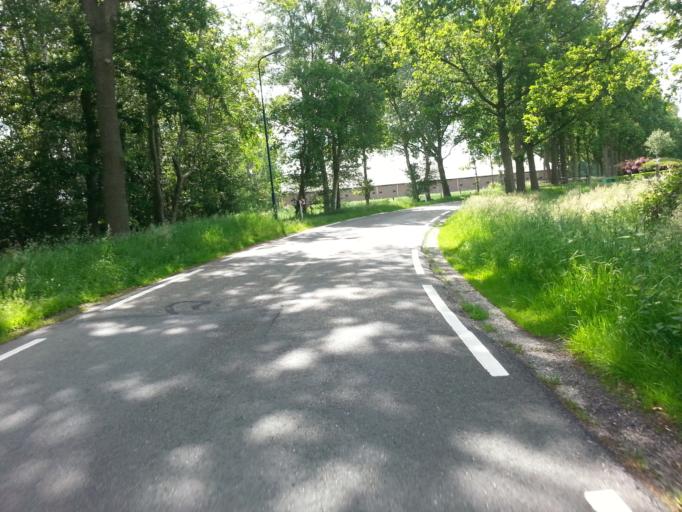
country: NL
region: Utrecht
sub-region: Gemeente Leusden
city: Leusden
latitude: 52.0964
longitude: 5.4748
